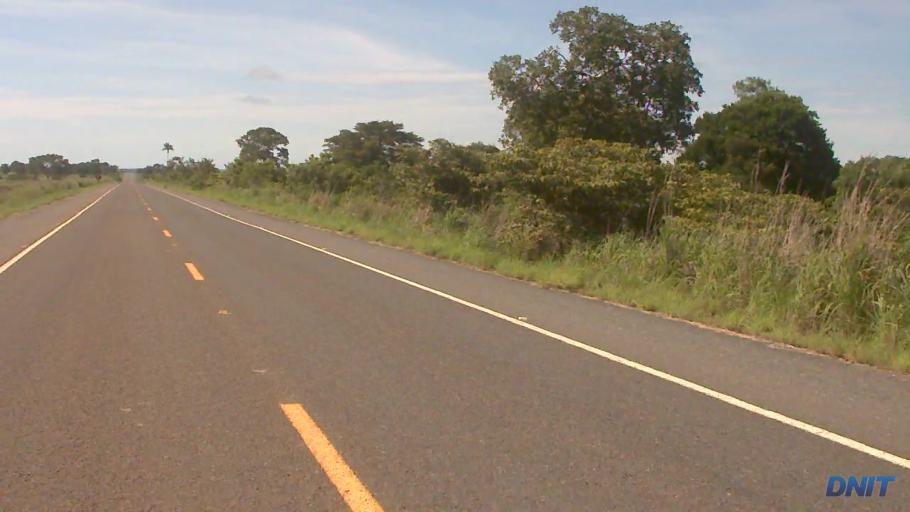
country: BR
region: Goias
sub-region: Sao Miguel Do Araguaia
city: Sao Miguel do Araguaia
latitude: -13.4413
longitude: -50.1233
